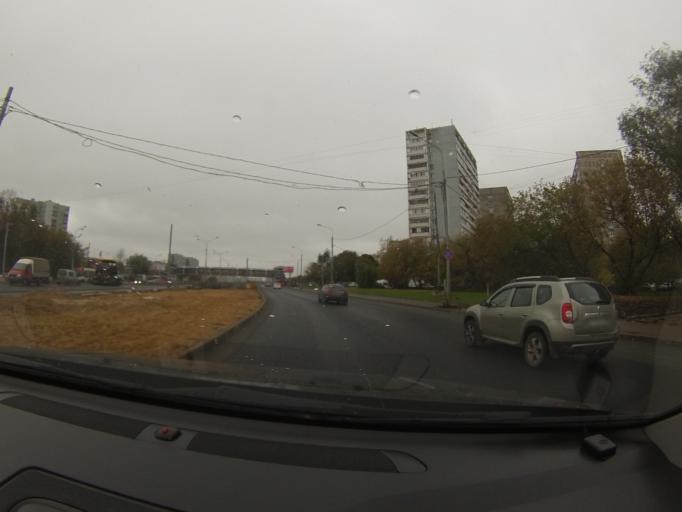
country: RU
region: Moscow
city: Amin'yevo
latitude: 55.7019
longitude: 37.4591
